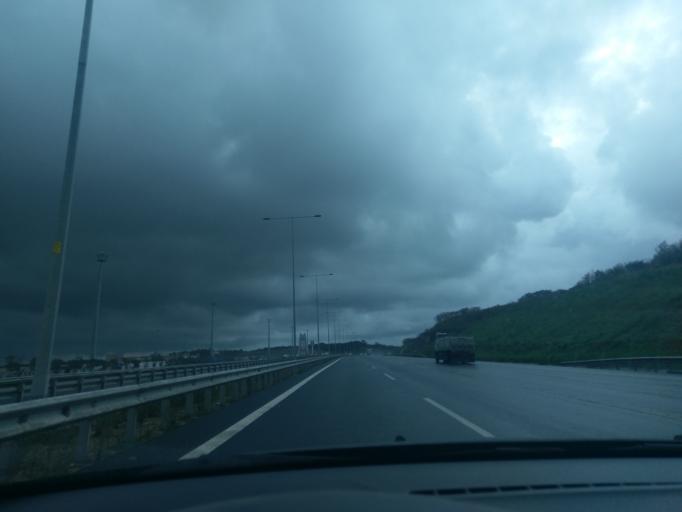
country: TR
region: Istanbul
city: Kemerburgaz
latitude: 41.2354
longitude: 28.9042
